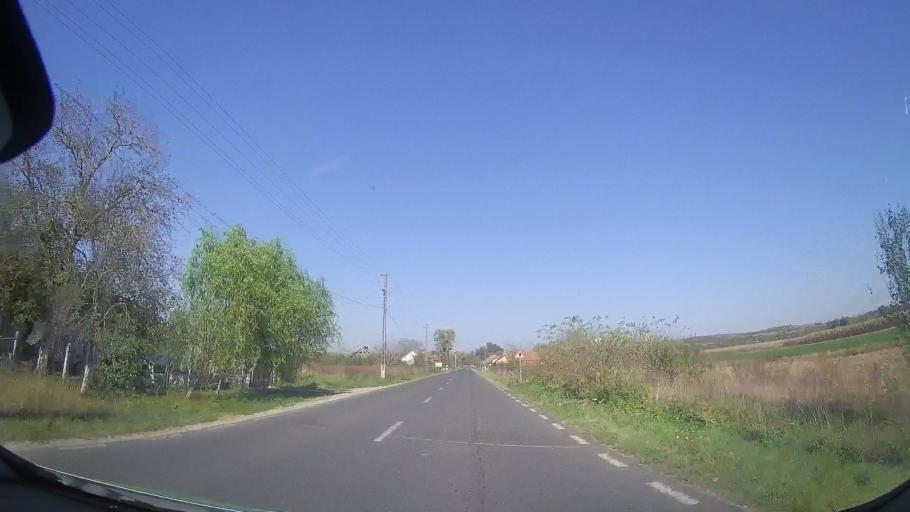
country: RO
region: Timis
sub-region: Comuna Balint
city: Balint
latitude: 45.8070
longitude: 21.8605
